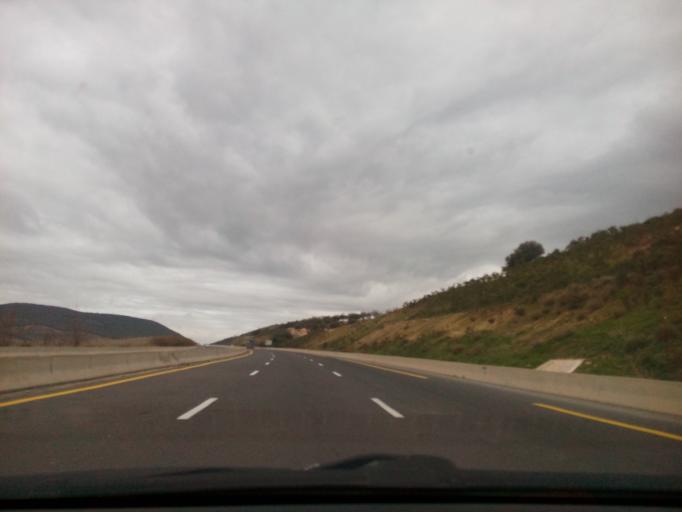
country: DZ
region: Sidi Bel Abbes
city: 'Ain el Berd
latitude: 35.3590
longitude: -0.5078
